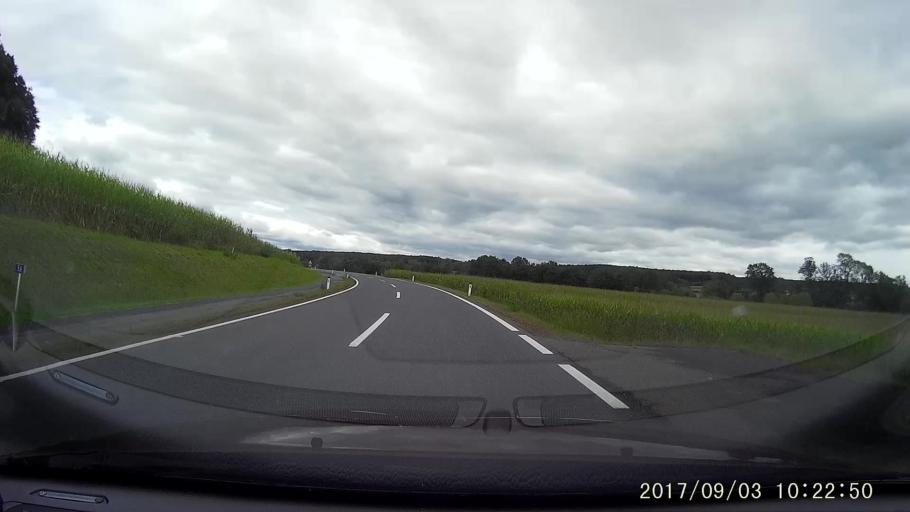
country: AT
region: Styria
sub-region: Politischer Bezirk Suedoststeiermark
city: Breitenfeld an der Rittschein
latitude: 47.0452
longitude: 15.9314
